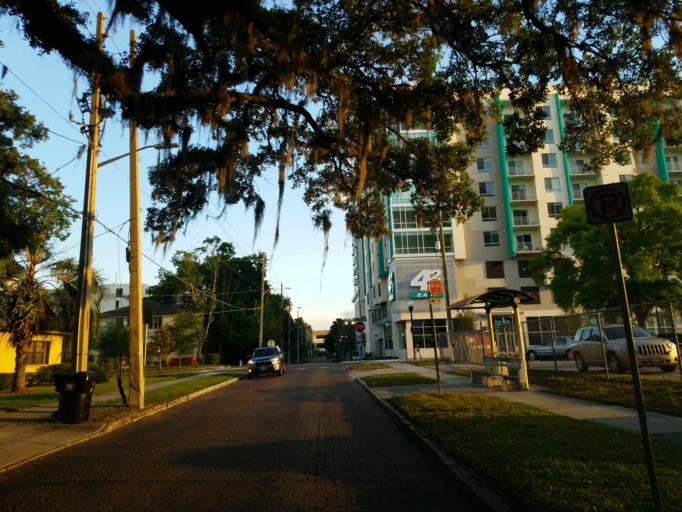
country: US
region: Florida
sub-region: Orange County
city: Orlando
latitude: 28.5409
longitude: -81.3713
